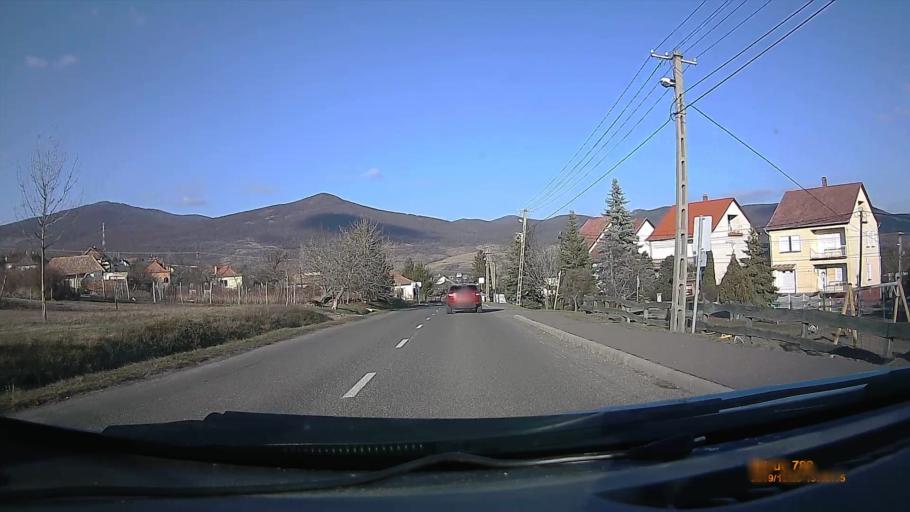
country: HU
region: Heves
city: Abasar
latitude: 47.8183
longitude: 20.0535
